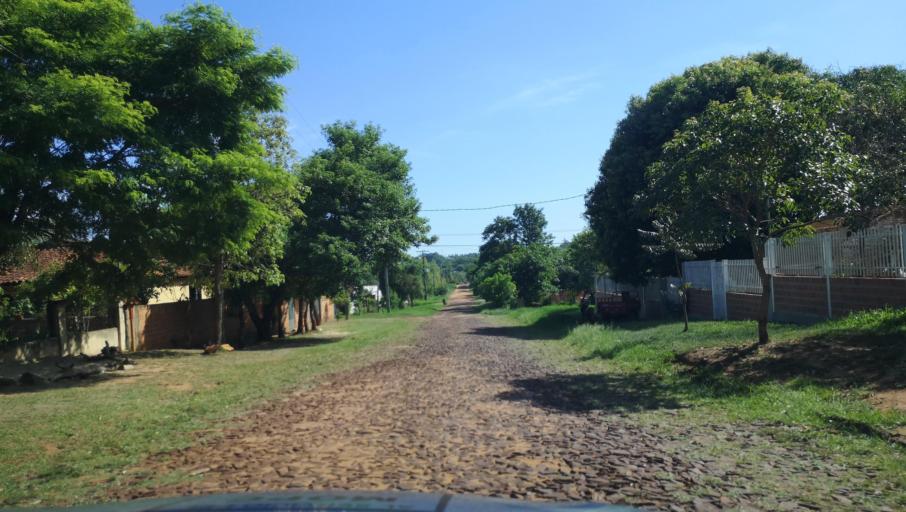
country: PY
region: Misiones
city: Santa Maria
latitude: -26.8840
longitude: -57.0209
